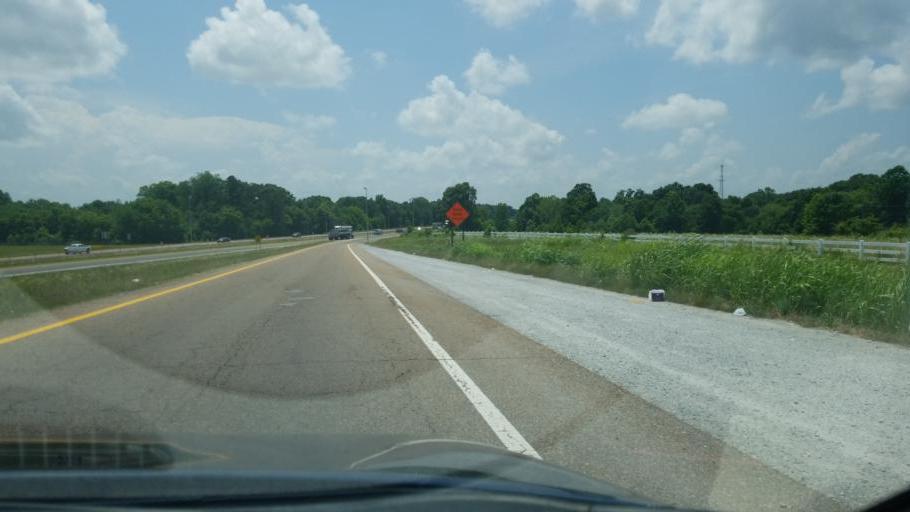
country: US
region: Tennessee
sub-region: Madison County
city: Jackson
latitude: 35.6818
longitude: -88.7429
